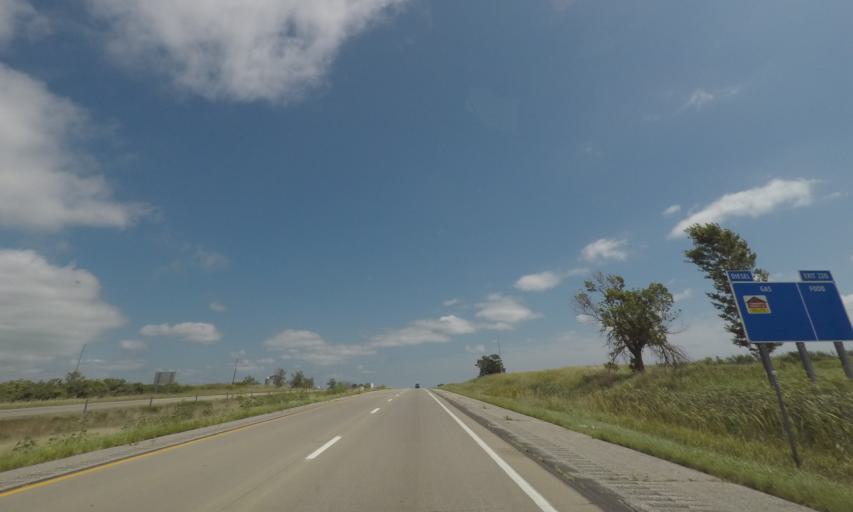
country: US
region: Iowa
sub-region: Iowa County
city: Williamsburg
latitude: 41.6871
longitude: -92.0365
